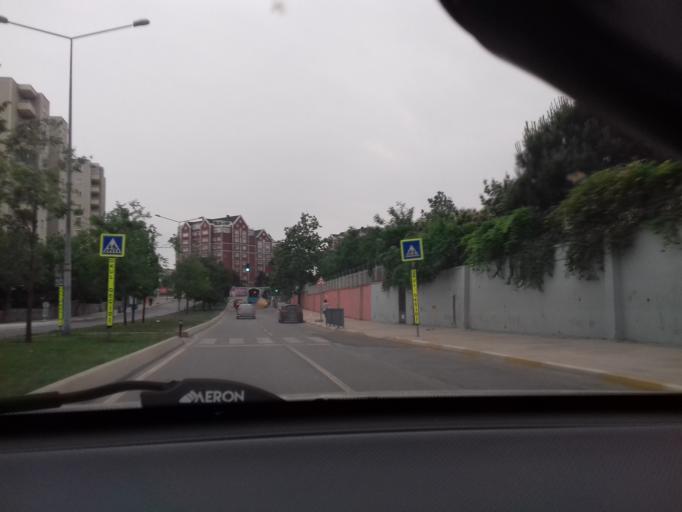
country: TR
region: Istanbul
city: Sultanbeyli
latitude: 40.9295
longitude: 29.2971
